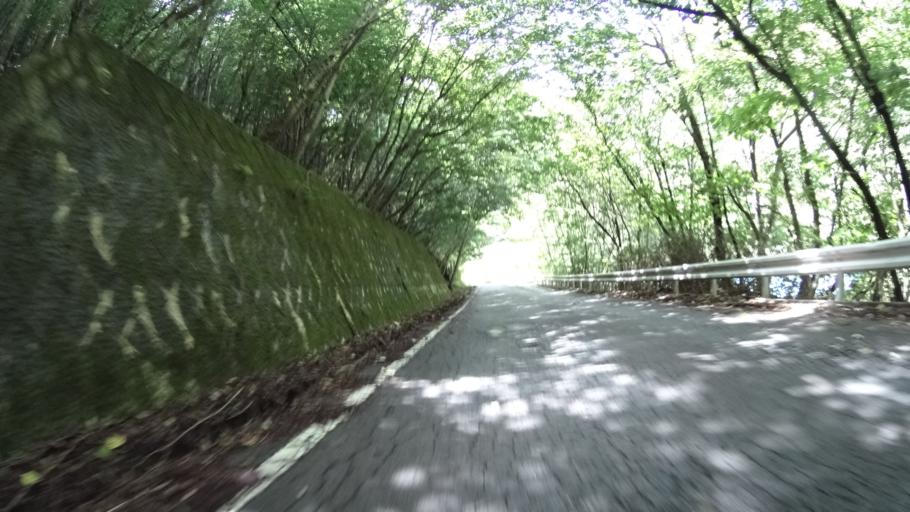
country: JP
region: Yamanashi
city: Enzan
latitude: 35.6752
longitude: 138.8074
